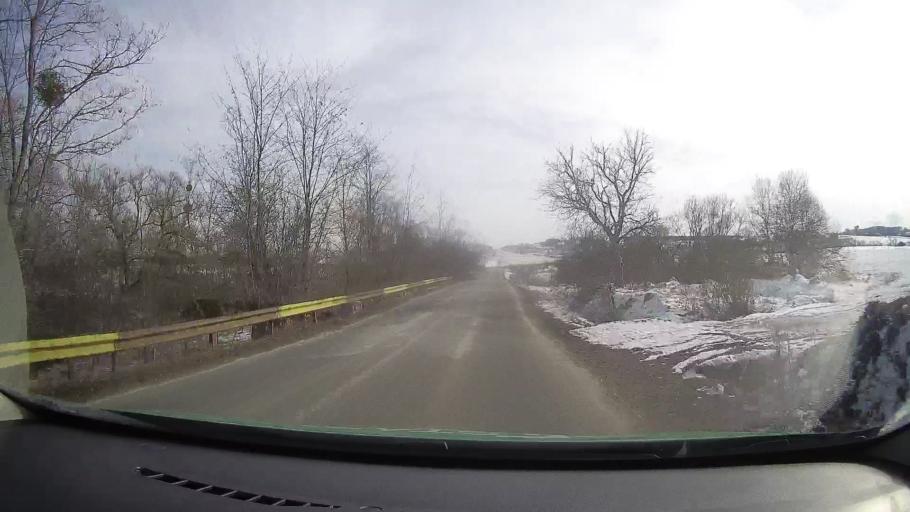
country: RO
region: Mures
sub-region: Comuna Apold
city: Apold
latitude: 46.1140
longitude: 24.8280
